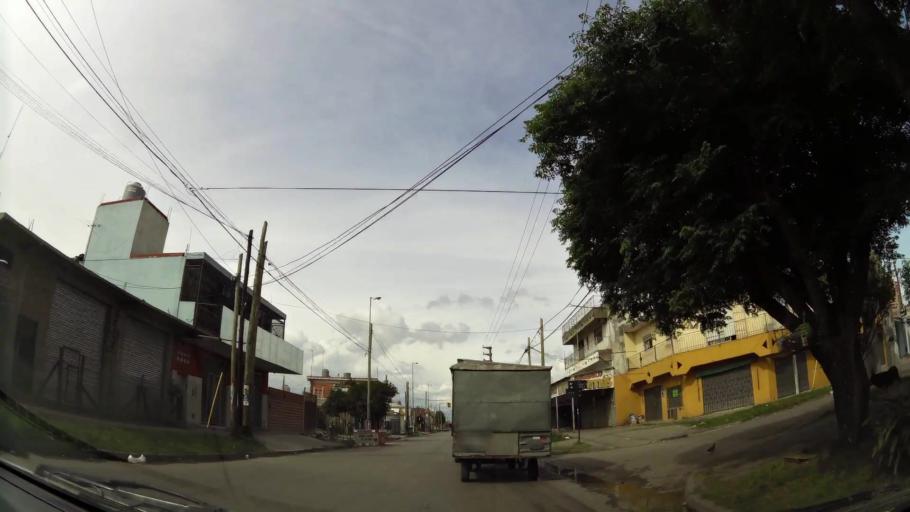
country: AR
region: Buenos Aires
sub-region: Partido de Quilmes
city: Quilmes
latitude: -34.7682
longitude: -58.2566
